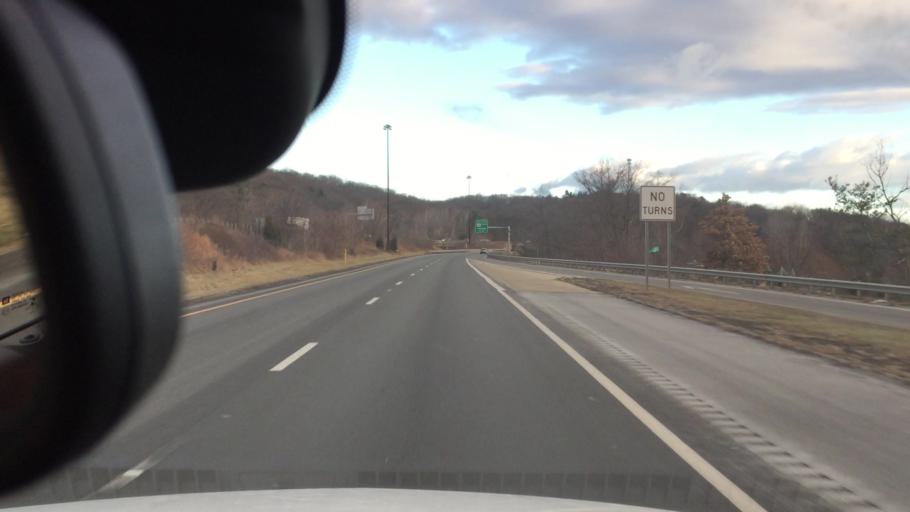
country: US
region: Massachusetts
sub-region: Hampden County
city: Holyoke
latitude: 42.2022
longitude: -72.6385
